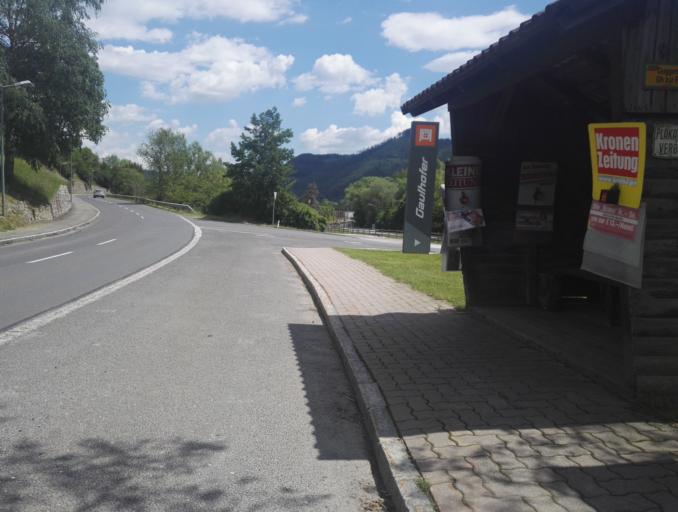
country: AT
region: Styria
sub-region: Politischer Bezirk Graz-Umgebung
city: Ubelbach
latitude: 47.2192
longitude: 15.2557
